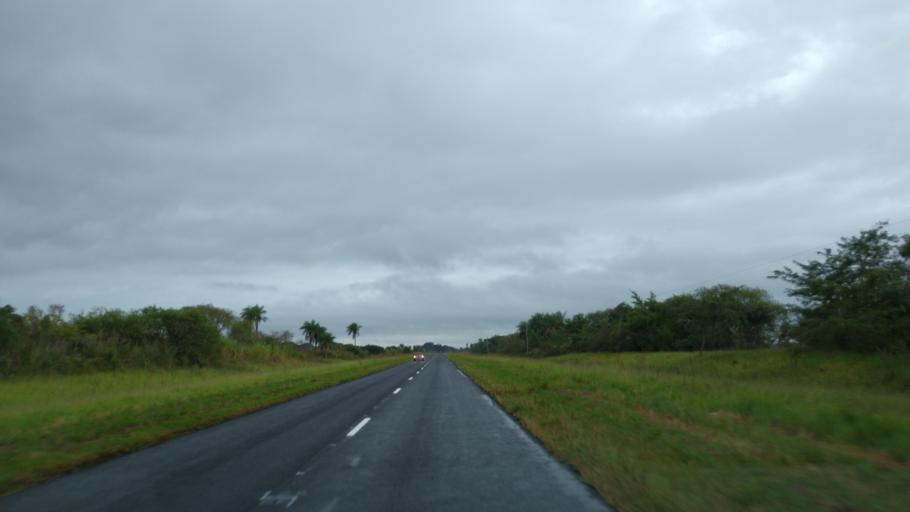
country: AR
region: Corrientes
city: Loreto
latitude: -27.7006
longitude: -57.2238
